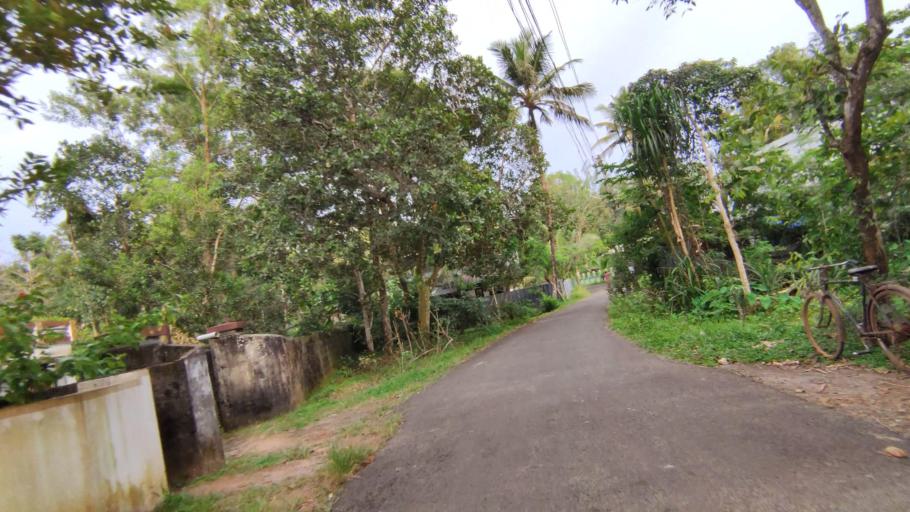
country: IN
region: Kerala
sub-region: Alappuzha
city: Shertallai
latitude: 9.6194
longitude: 76.3439
